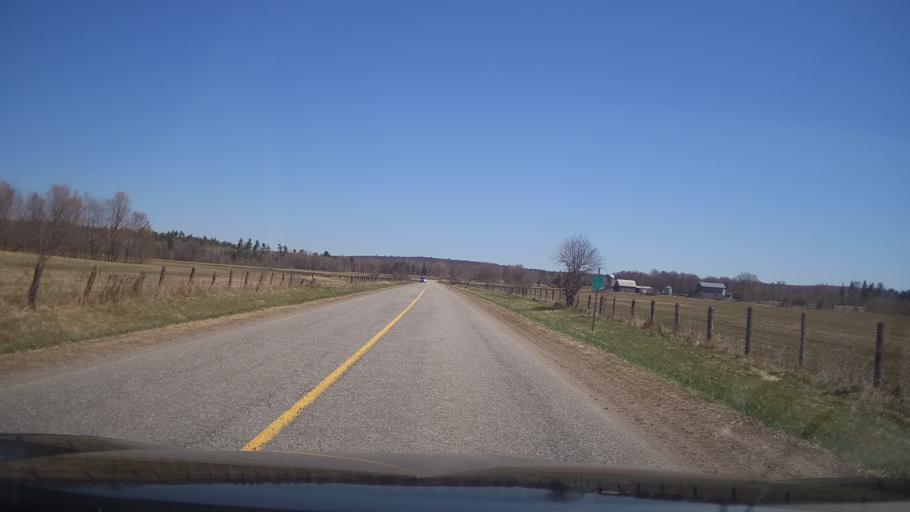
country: CA
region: Quebec
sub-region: Outaouais
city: Shawville
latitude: 45.5479
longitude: -76.3863
